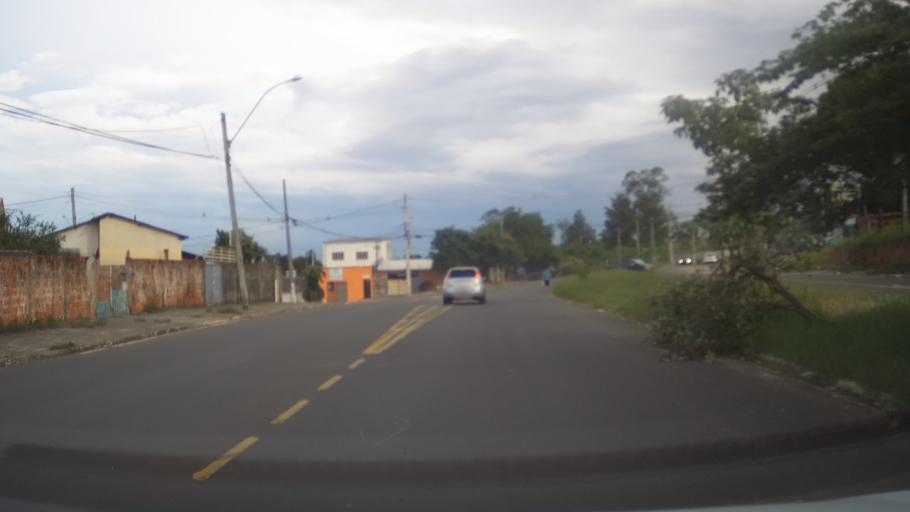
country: BR
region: Sao Paulo
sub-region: Hortolandia
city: Hortolandia
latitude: -22.9553
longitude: -47.2156
